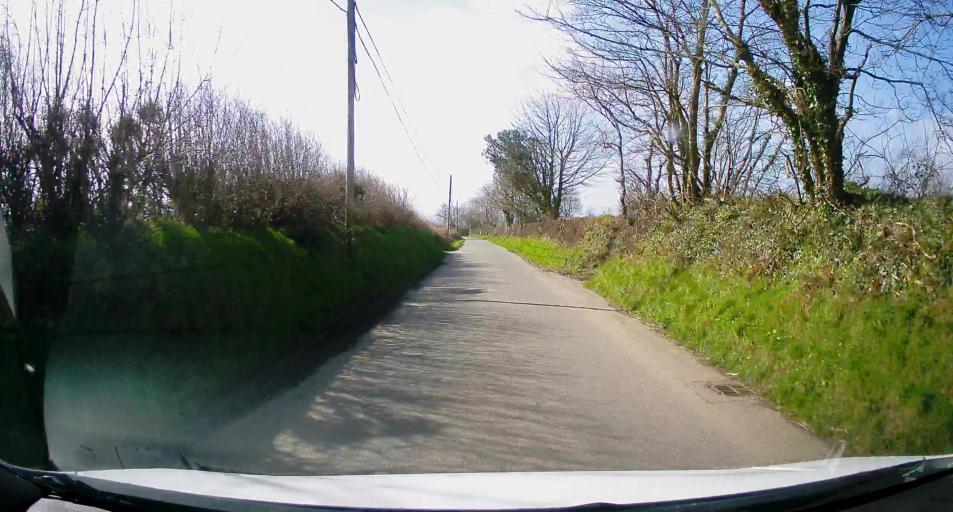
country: GB
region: Wales
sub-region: County of Ceredigion
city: Aberporth
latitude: 52.0706
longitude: -4.5622
